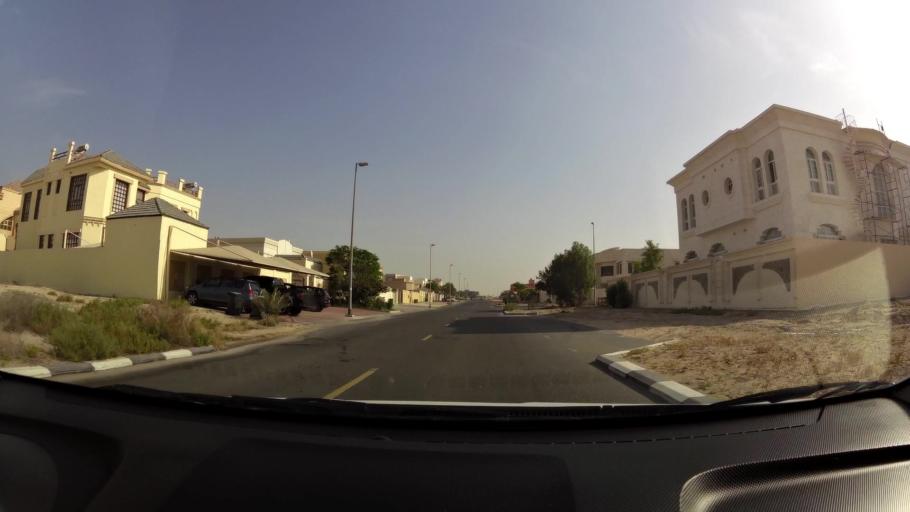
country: AE
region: Ash Shariqah
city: Sharjah
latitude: 25.2406
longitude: 55.4144
